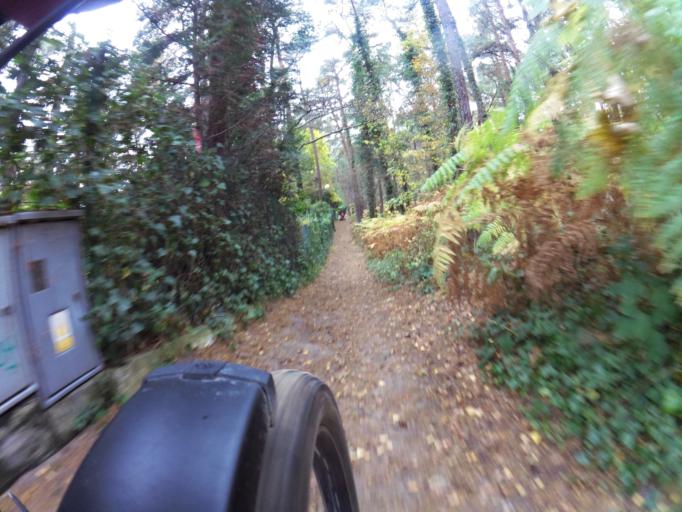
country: PL
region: Pomeranian Voivodeship
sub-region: Powiat pucki
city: Jastarnia
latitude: 54.6848
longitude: 18.7088
